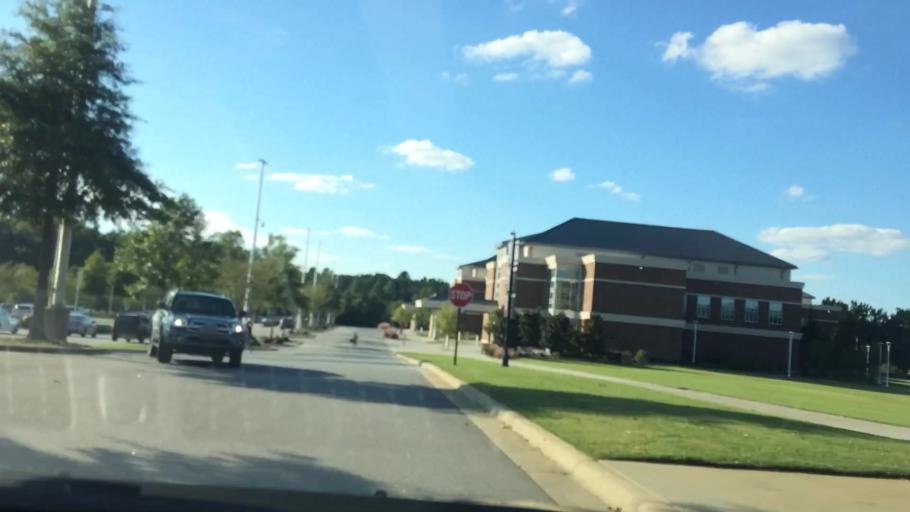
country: US
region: North Carolina
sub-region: Pitt County
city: Greenville
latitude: 35.6101
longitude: -77.4074
